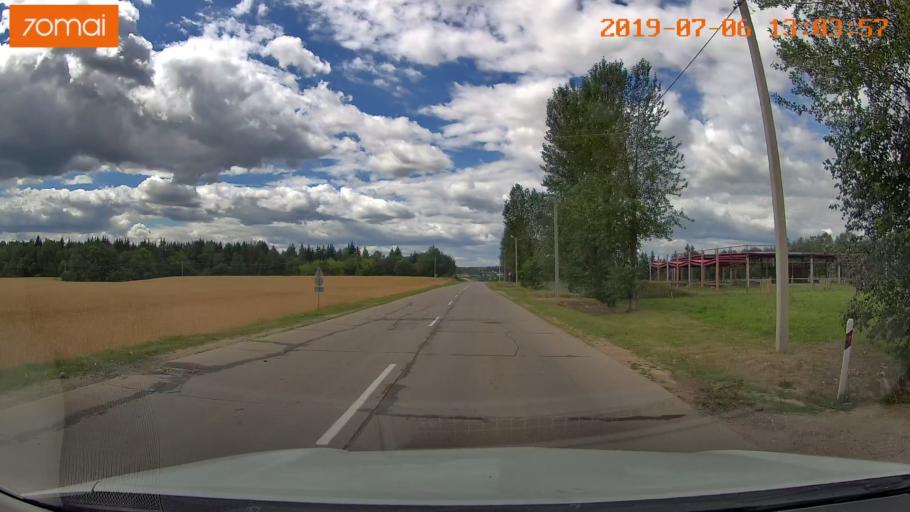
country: BY
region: Minsk
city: Dzyarzhynsk
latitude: 53.6905
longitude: 27.0932
